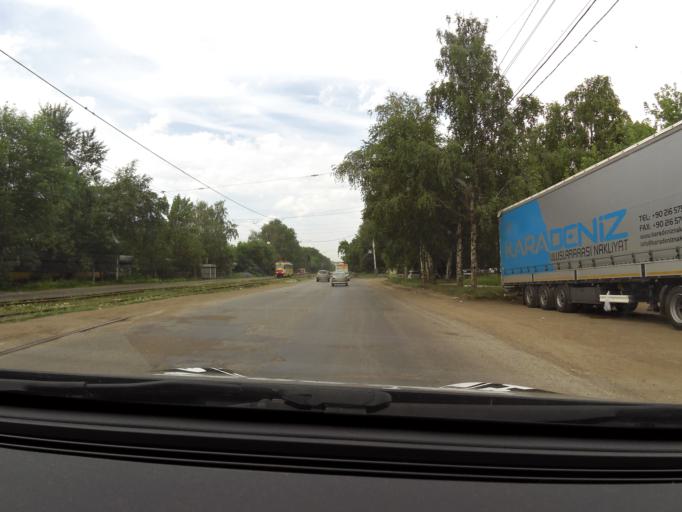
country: RU
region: Bashkortostan
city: Ufa
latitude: 54.7989
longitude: 56.0886
